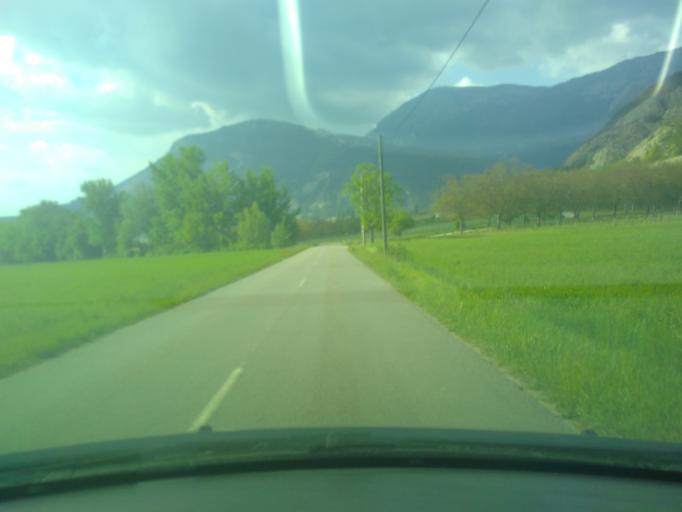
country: FR
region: Rhone-Alpes
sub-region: Departement de la Drome
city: Die
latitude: 44.6745
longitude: 5.4739
